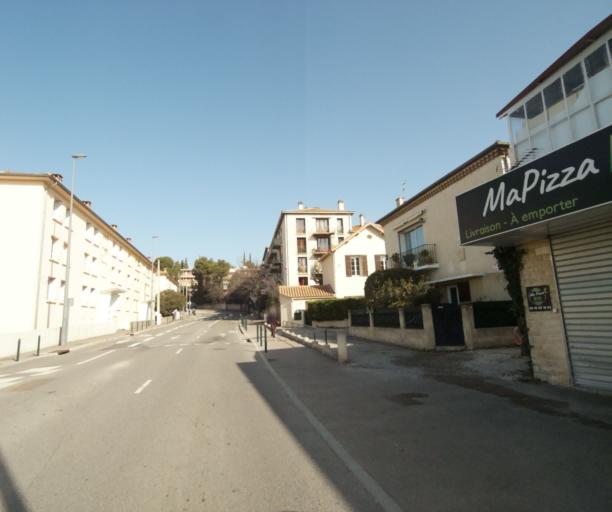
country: FR
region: Provence-Alpes-Cote d'Azur
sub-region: Departement des Bouches-du-Rhone
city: Aix-en-Provence
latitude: 43.5365
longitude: 5.4448
